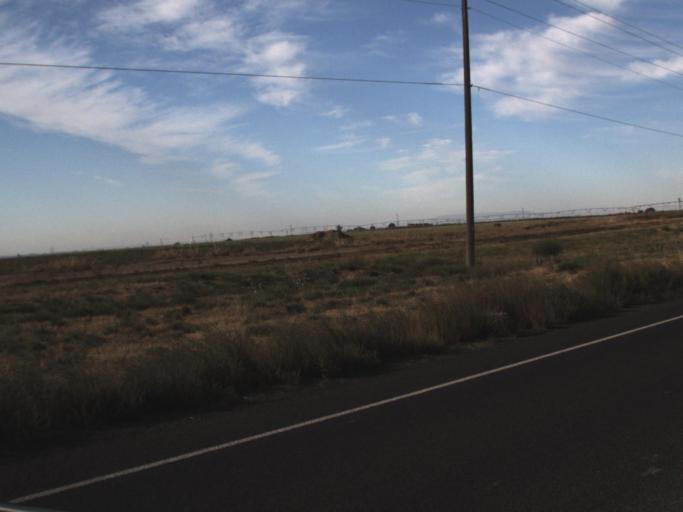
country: US
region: Washington
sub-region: Franklin County
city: Connell
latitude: 46.6636
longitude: -118.9335
